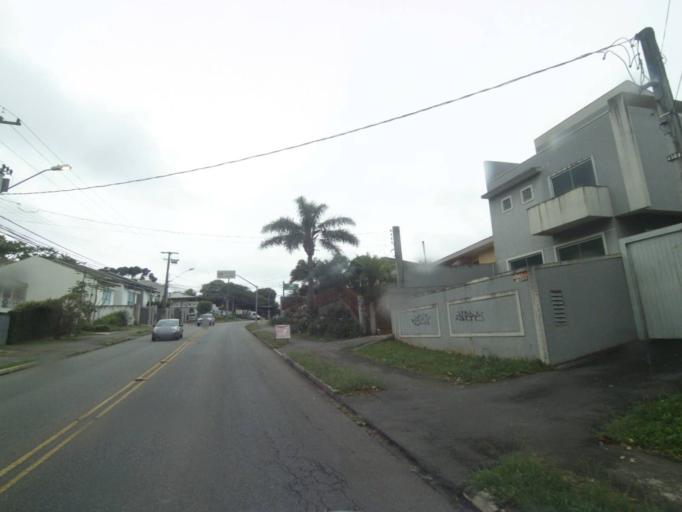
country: BR
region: Parana
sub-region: Curitiba
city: Curitiba
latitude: -25.4201
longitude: -49.3241
